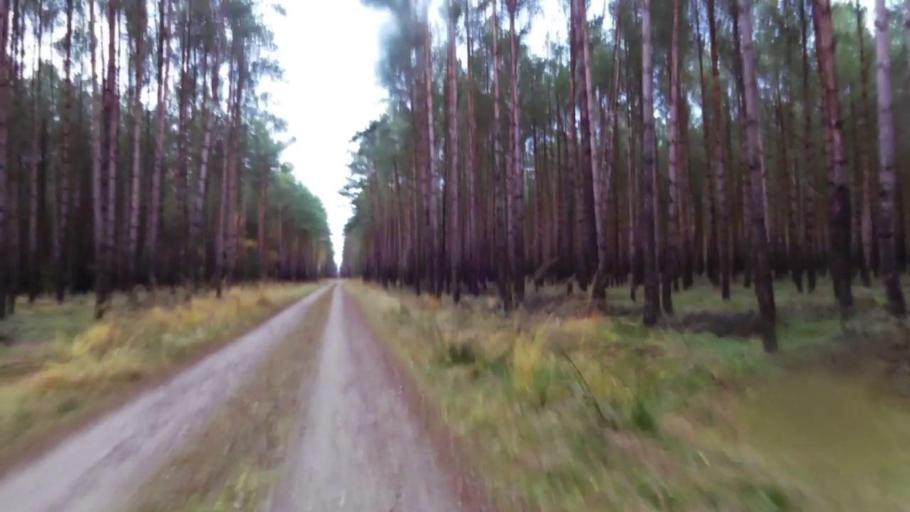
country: PL
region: West Pomeranian Voivodeship
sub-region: Powiat goleniowski
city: Stepnica
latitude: 53.6350
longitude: 14.7132
